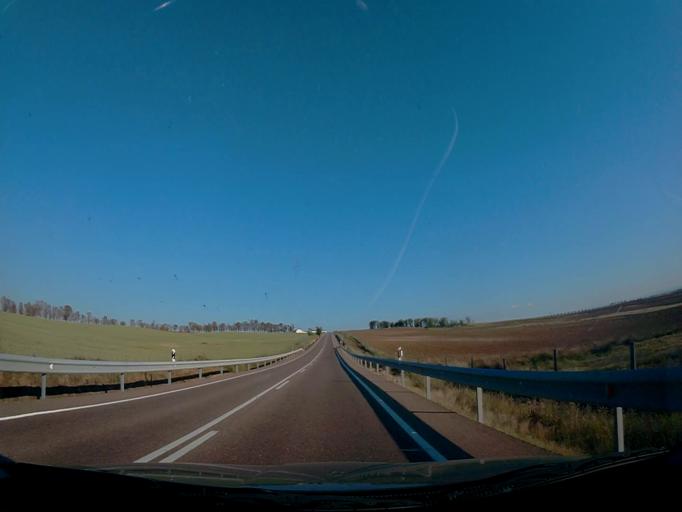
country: ES
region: Castille-La Mancha
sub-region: Province of Toledo
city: Maqueda
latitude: 40.0979
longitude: -4.3925
